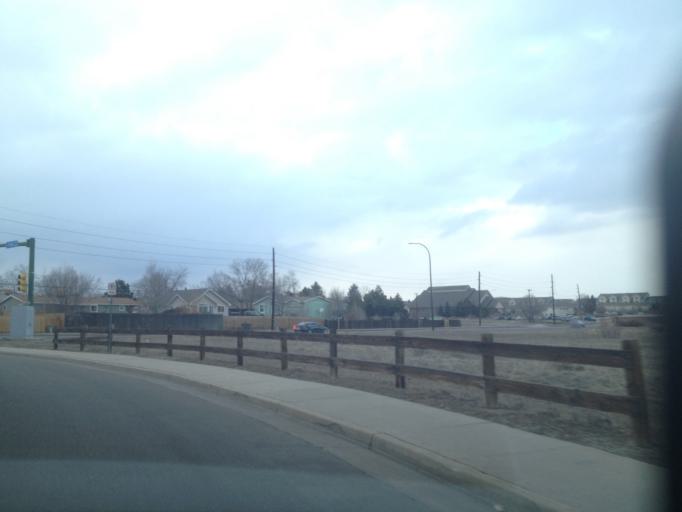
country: US
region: Colorado
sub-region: Adams County
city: Westminster
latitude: 39.8200
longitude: -105.0526
